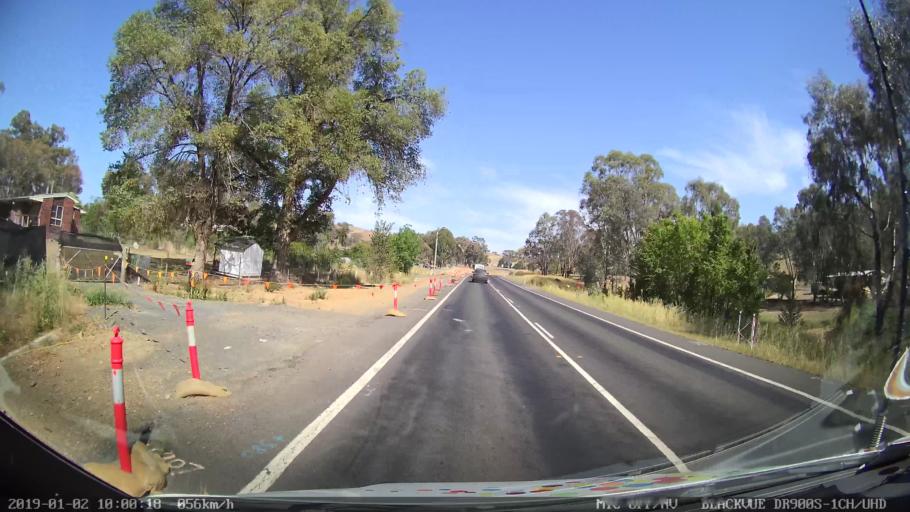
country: AU
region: New South Wales
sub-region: Gundagai
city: Gundagai
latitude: -35.1956
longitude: 148.1332
